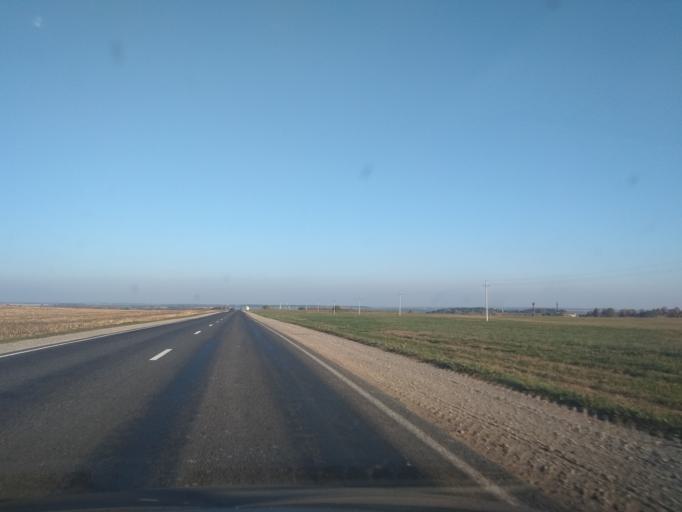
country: BY
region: Grodnenskaya
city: Svislach
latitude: 53.1310
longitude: 24.1803
